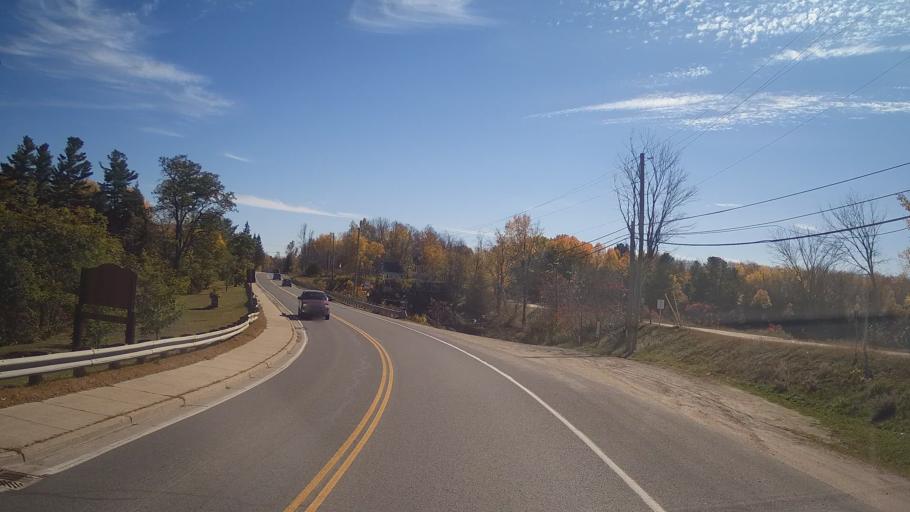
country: CA
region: Ontario
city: Perth
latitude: 44.7678
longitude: -76.6901
